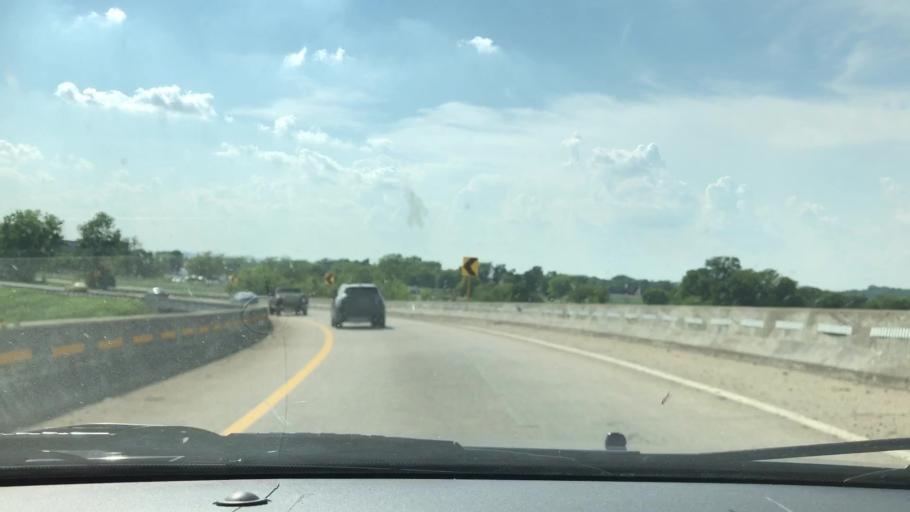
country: US
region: Tennessee
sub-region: Maury County
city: Spring Hill
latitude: 35.7400
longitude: -86.9468
